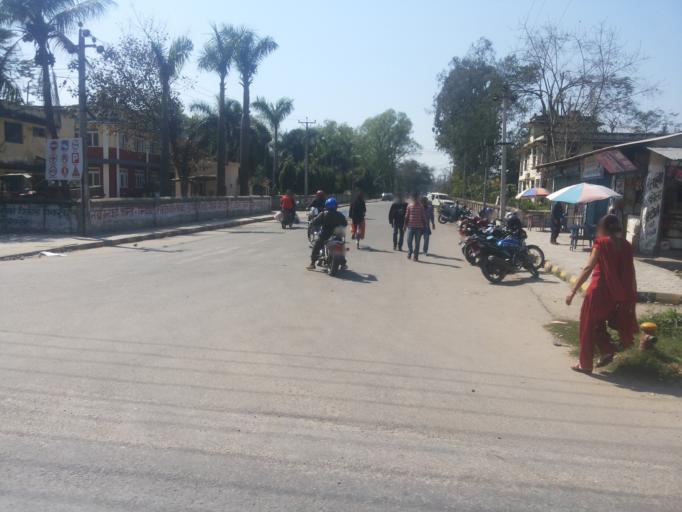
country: NP
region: Central Region
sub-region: Narayani Zone
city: Bharatpur
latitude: 27.6814
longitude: 84.4394
